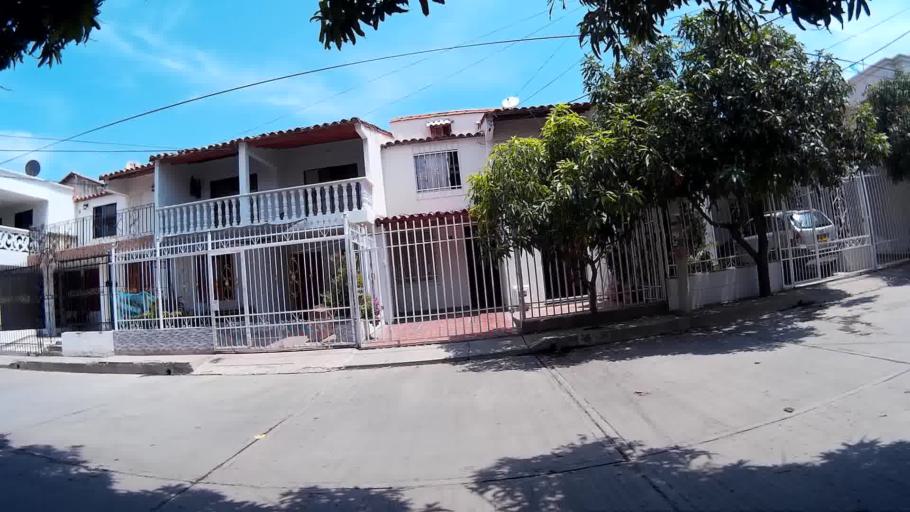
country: CO
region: Magdalena
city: Santa Marta
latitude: 11.2260
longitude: -74.2021
